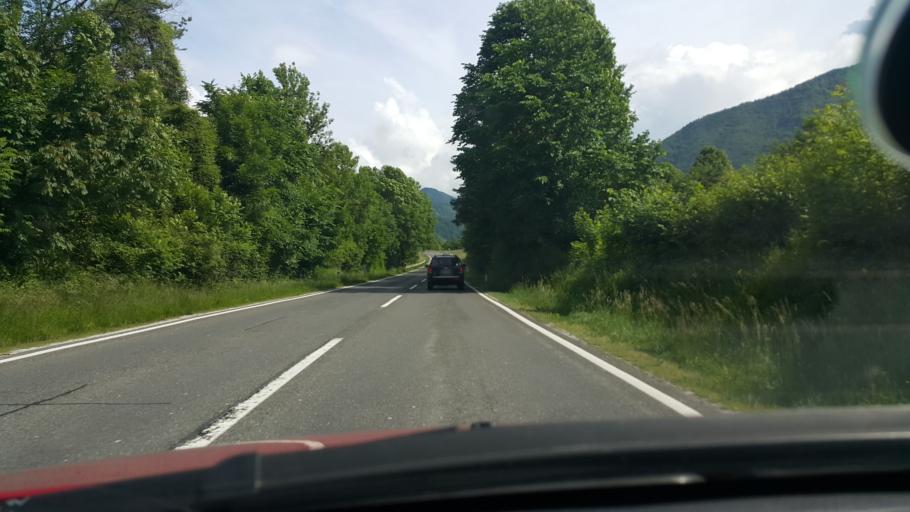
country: SI
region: Trzic
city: Bistrica pri Trzicu
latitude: 46.3380
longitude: 14.2838
